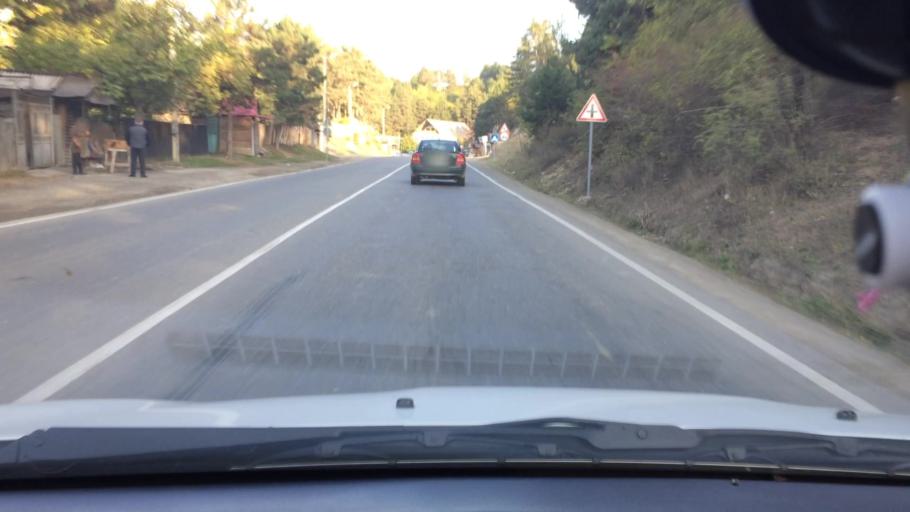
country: GE
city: Surami
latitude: 42.0264
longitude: 43.5613
